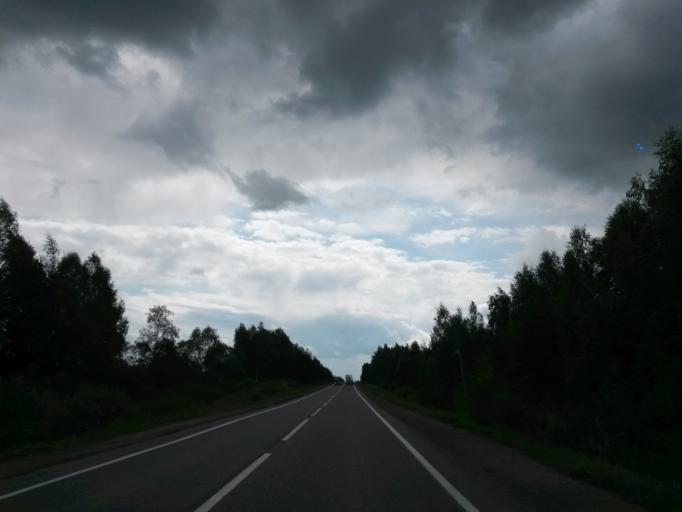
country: RU
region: Jaroslavl
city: Gavrilov-Yam
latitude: 57.3673
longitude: 39.9077
